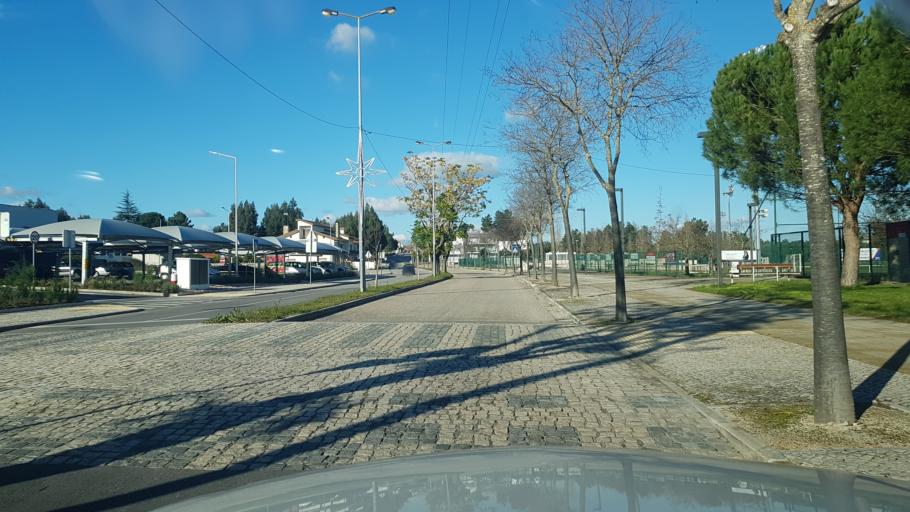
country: PT
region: Santarem
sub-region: Entroncamento
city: Entroncamento
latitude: 39.4737
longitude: -8.4677
